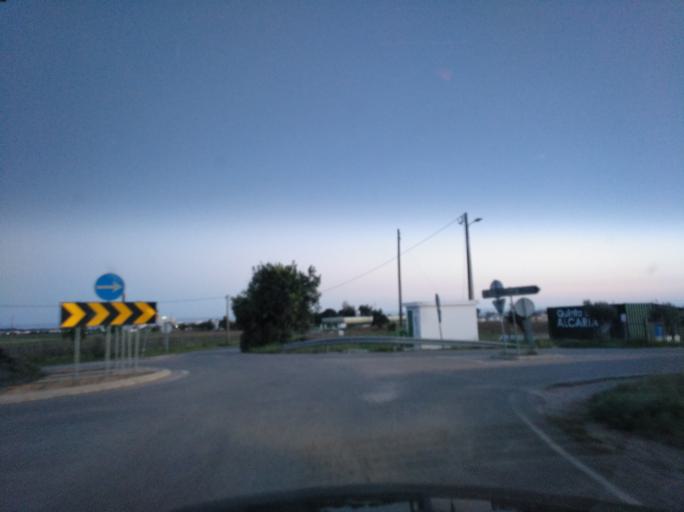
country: PT
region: Faro
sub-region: Vila Real de Santo Antonio
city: Monte Gordo
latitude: 37.1931
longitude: -7.5140
